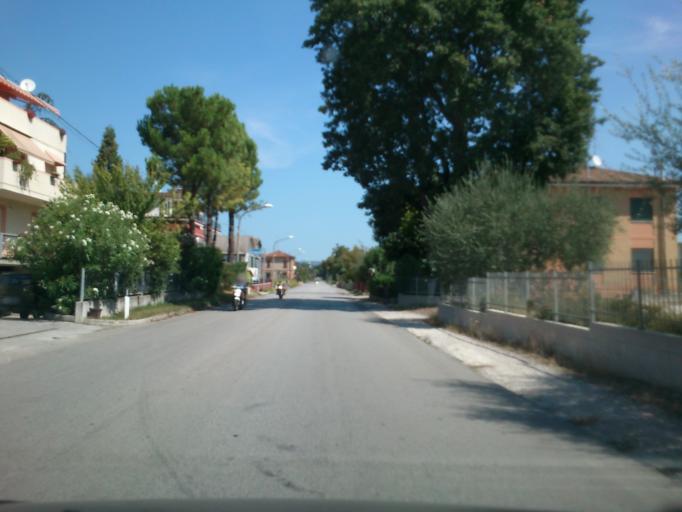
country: IT
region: The Marches
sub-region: Provincia di Pesaro e Urbino
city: Calcinelli
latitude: 43.7578
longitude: 12.9243
